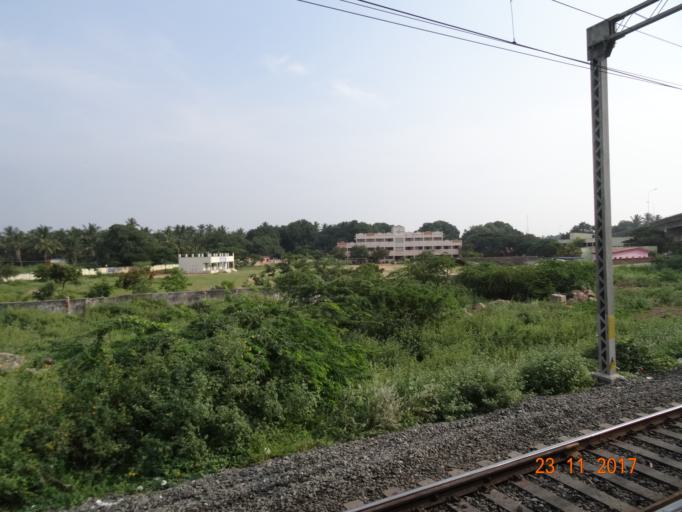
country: IN
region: Tamil Nadu
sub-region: Coimbatore
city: Irugur
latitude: 11.0142
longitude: 77.0668
